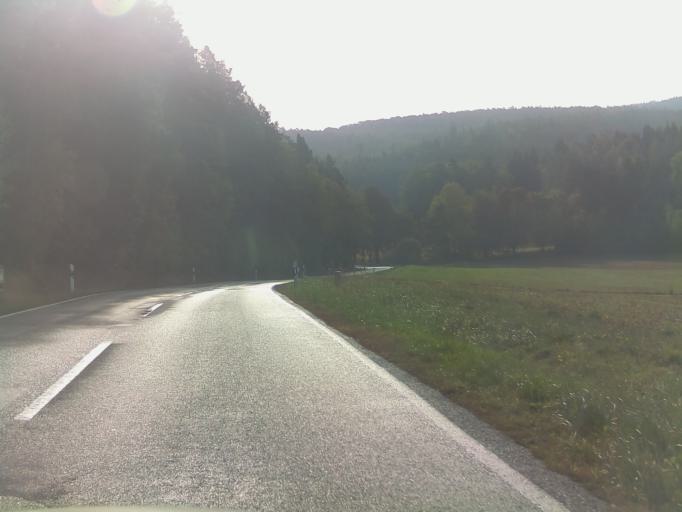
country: DE
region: Hesse
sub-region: Regierungsbezirk Kassel
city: Hosenfeld
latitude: 50.5062
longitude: 9.5049
